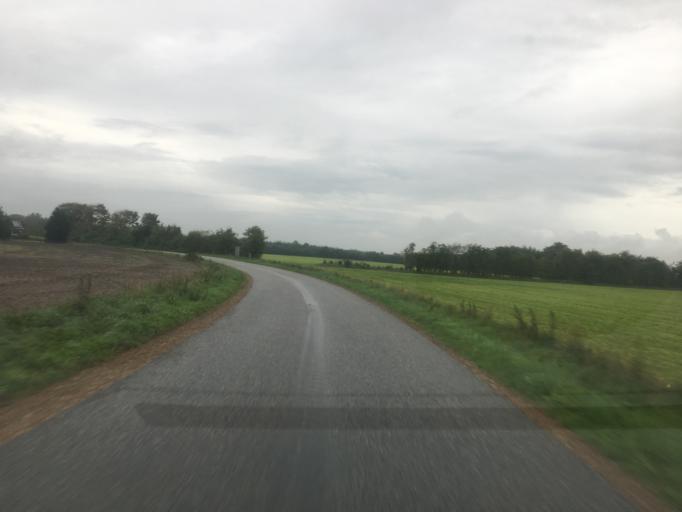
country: DK
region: South Denmark
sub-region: Tonder Kommune
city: Logumkloster
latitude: 55.0117
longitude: 9.0351
